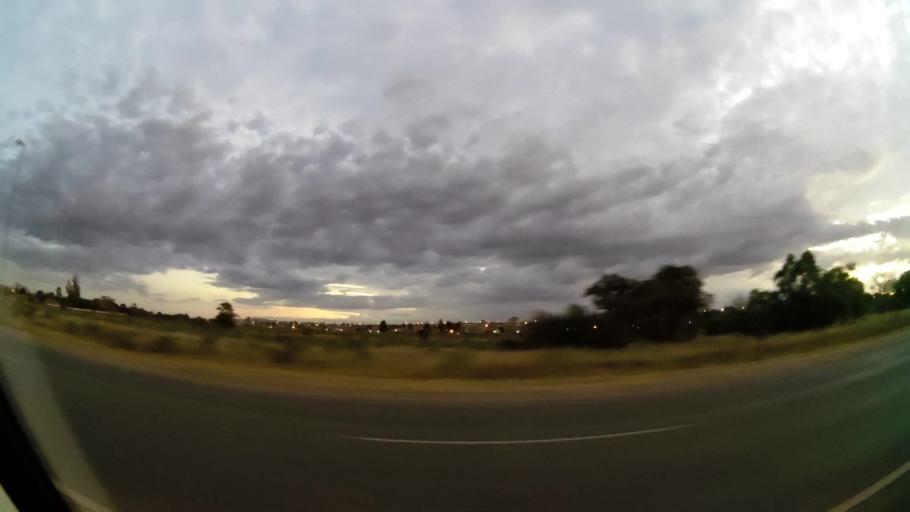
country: ZA
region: Limpopo
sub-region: Capricorn District Municipality
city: Polokwane
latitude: -23.8672
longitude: 29.4346
